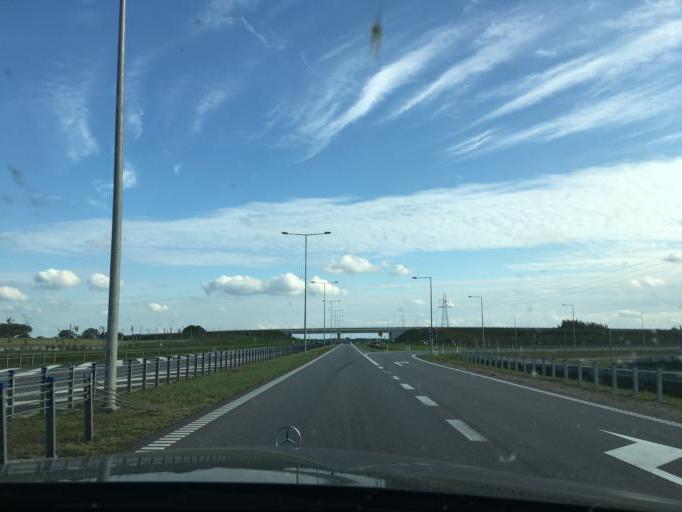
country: PL
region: Podlasie
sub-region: Powiat augustowski
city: Augustow
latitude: 53.8464
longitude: 22.9412
